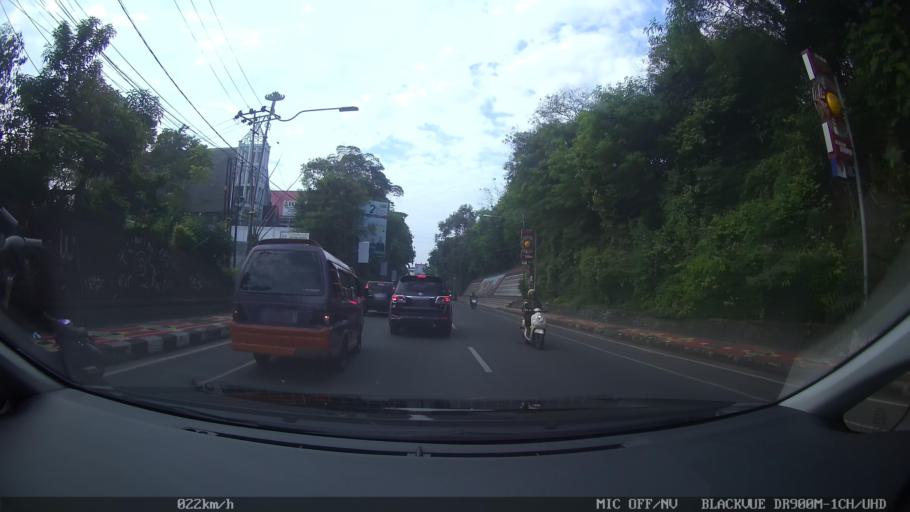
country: ID
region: Lampung
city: Bandarlampung
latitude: -5.4259
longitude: 105.2588
